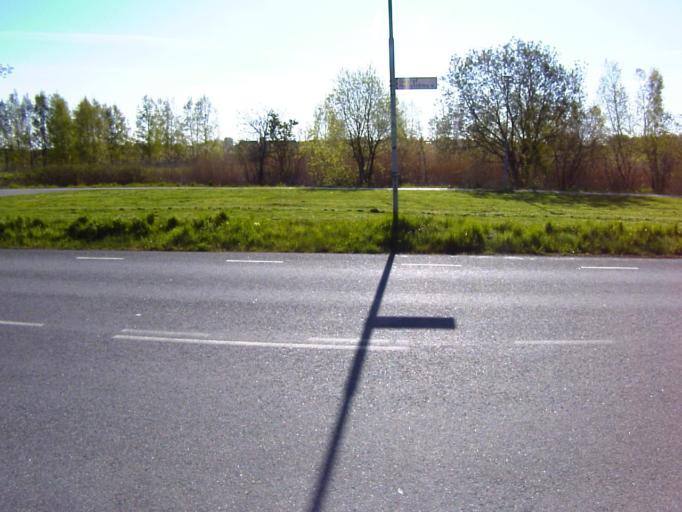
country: SE
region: Skane
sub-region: Kristianstads Kommun
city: Kristianstad
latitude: 56.0342
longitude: 14.1860
